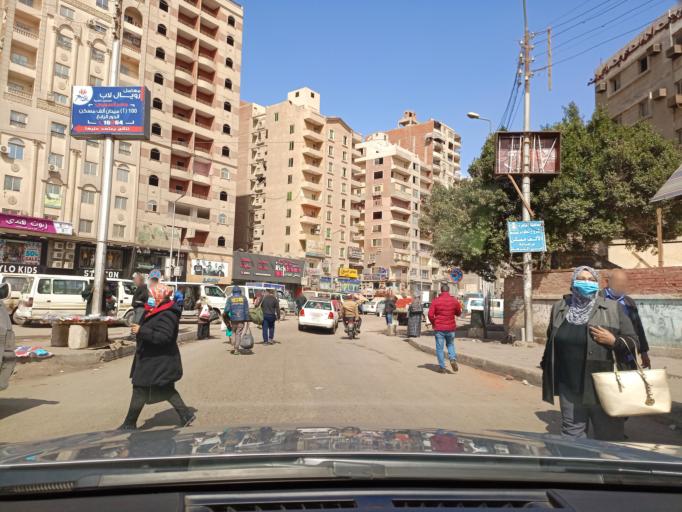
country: EG
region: Muhafazat al Qalyubiyah
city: Al Khankah
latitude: 30.1195
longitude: 31.3409
